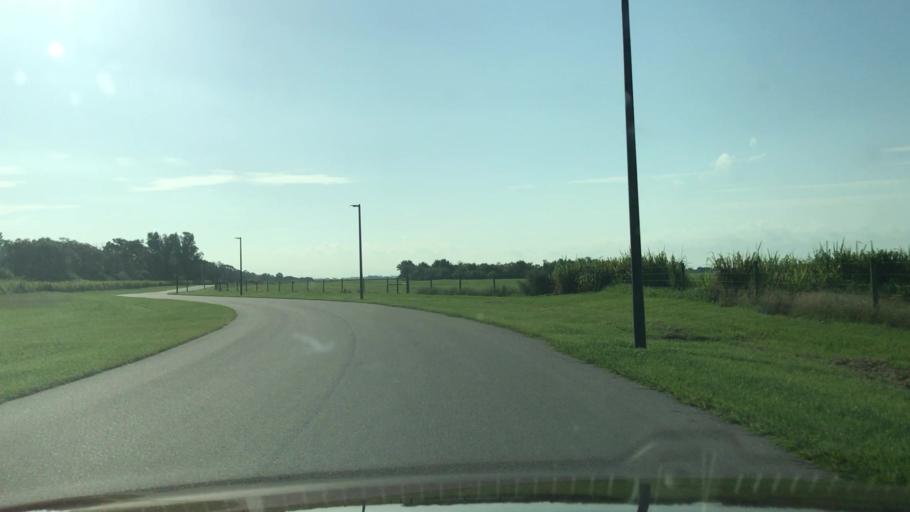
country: US
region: Florida
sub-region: Sarasota County
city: The Meadows
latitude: 27.4714
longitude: -82.3875
